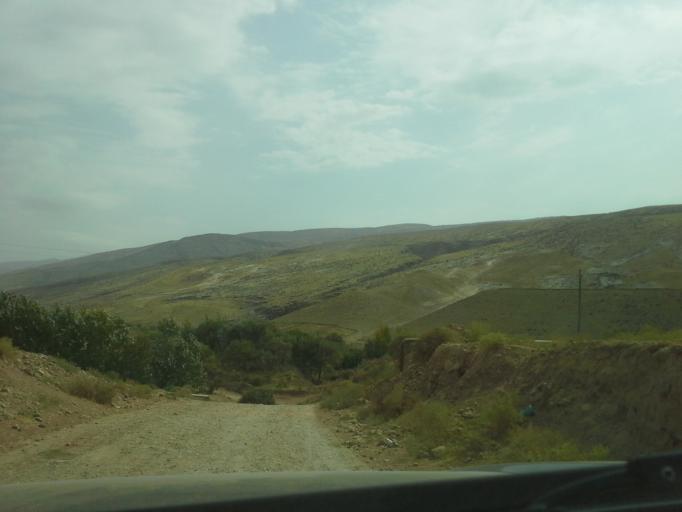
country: UZ
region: Qashqadaryo
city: Qorashina
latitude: 37.9338
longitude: 66.5070
